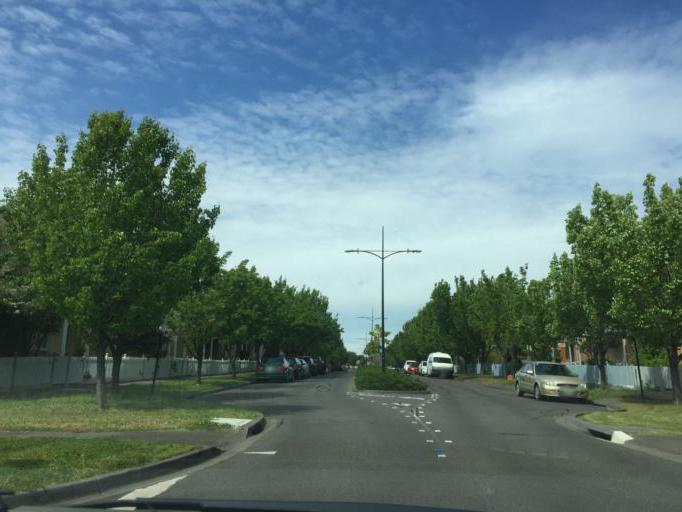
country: AU
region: Victoria
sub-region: Maribyrnong
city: Maidstone
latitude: -37.7724
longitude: 144.8774
